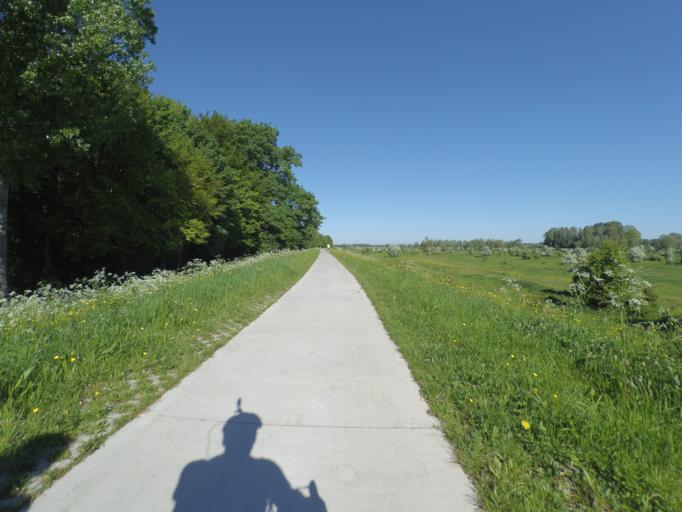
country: NL
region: Gelderland
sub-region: Gemeente Zutphen
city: Zutphen
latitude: 52.1067
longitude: 6.1989
